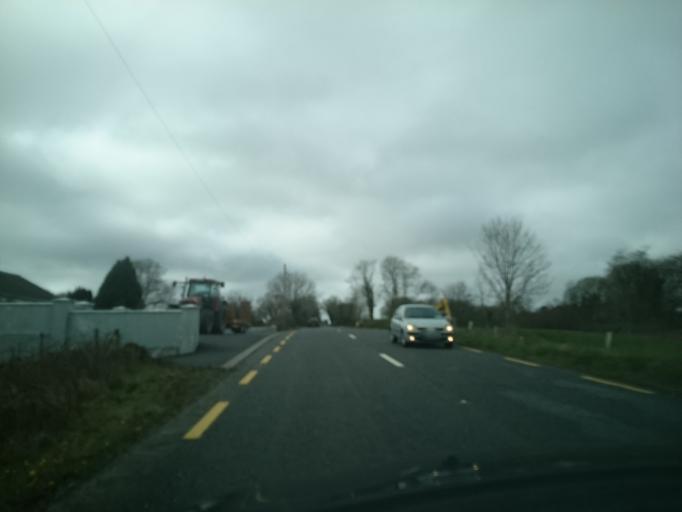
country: IE
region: Connaught
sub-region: Maigh Eo
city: Westport
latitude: 53.8045
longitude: -9.4604
